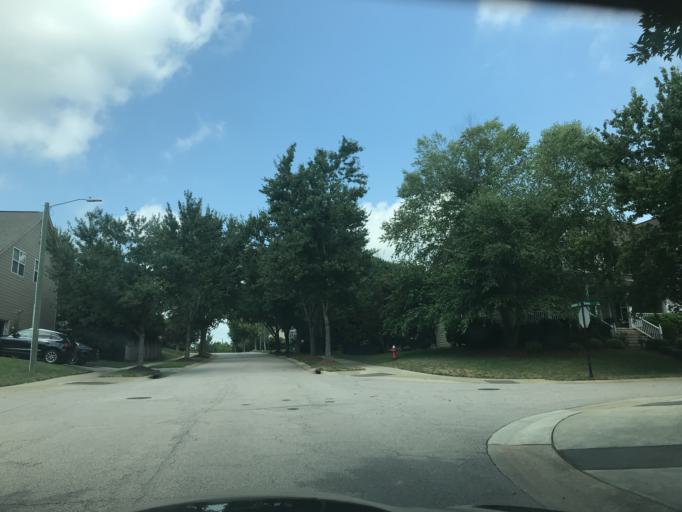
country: US
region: North Carolina
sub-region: Wake County
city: Wake Forest
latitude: 35.9281
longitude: -78.5659
